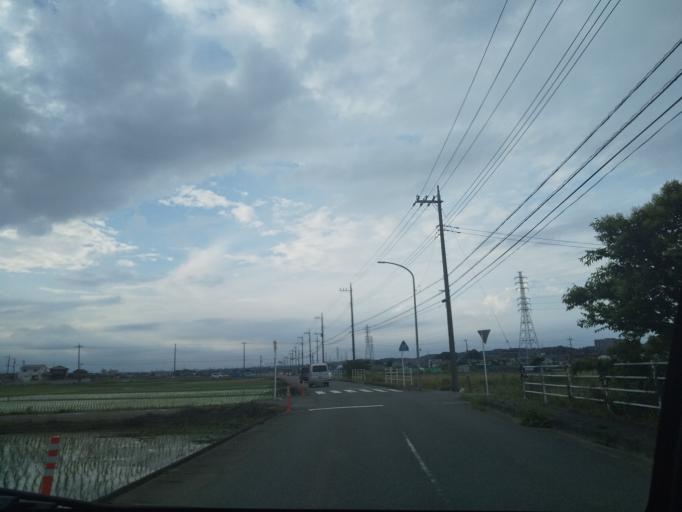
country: JP
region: Kanagawa
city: Zama
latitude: 35.4880
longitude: 139.3855
